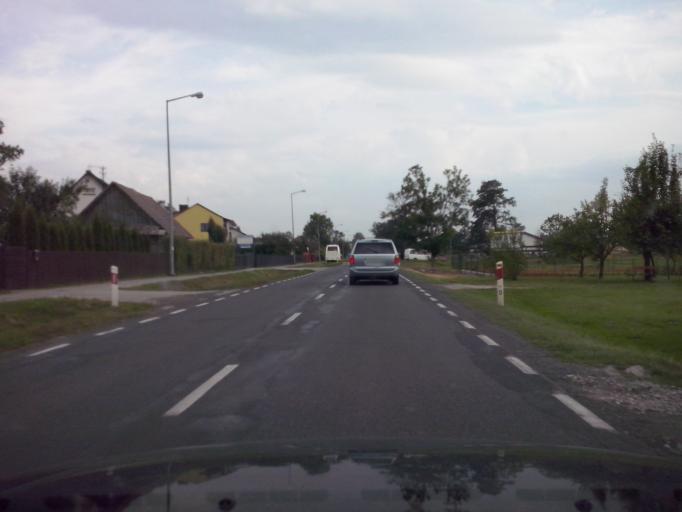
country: PL
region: Lublin Voivodeship
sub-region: Powiat bilgorajski
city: Bilgoraj
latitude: 50.5050
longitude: 22.7213
